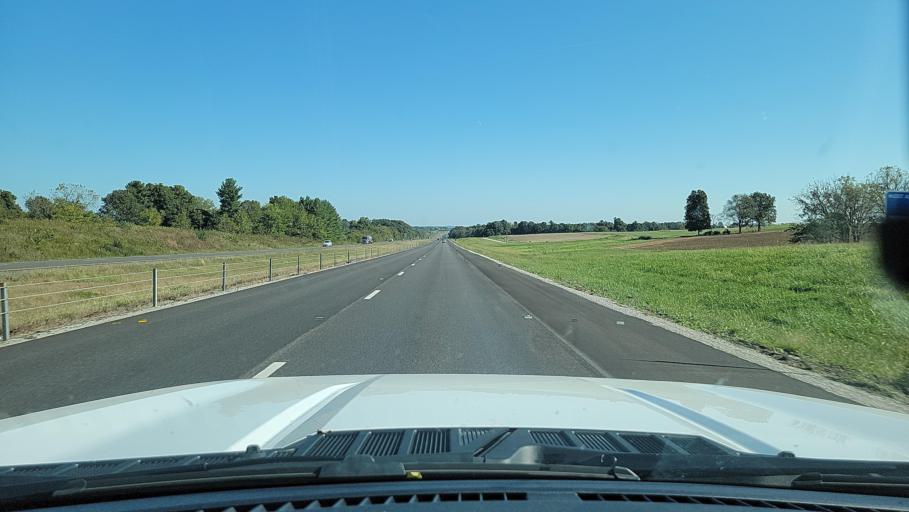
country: US
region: Missouri
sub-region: Perry County
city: Perryville
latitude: 37.6309
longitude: -89.8251
